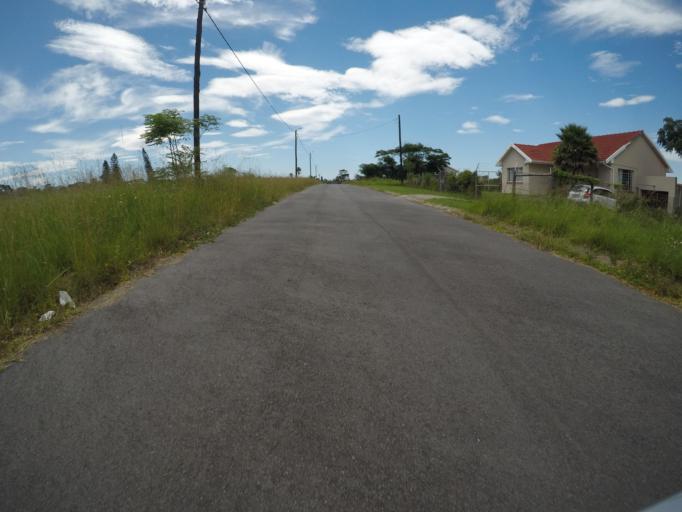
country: ZA
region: Eastern Cape
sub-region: Buffalo City Metropolitan Municipality
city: East London
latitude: -33.0404
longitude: 27.8564
